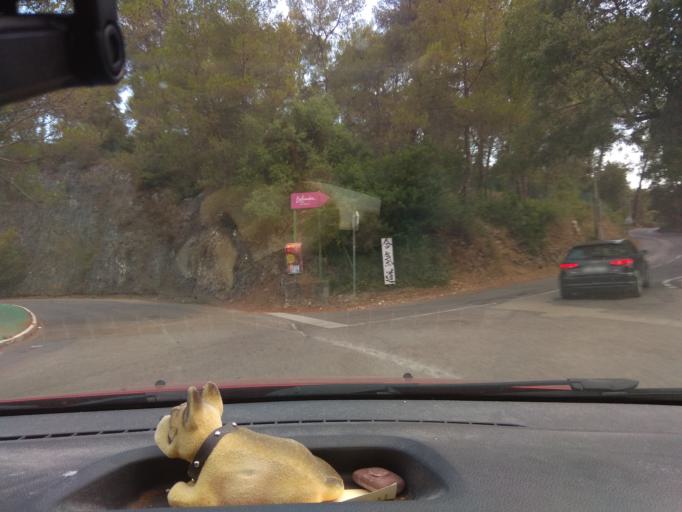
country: FR
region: Provence-Alpes-Cote d'Azur
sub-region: Departement des Alpes-Maritimes
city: La Colle-sur-Loup
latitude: 43.6851
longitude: 7.0991
